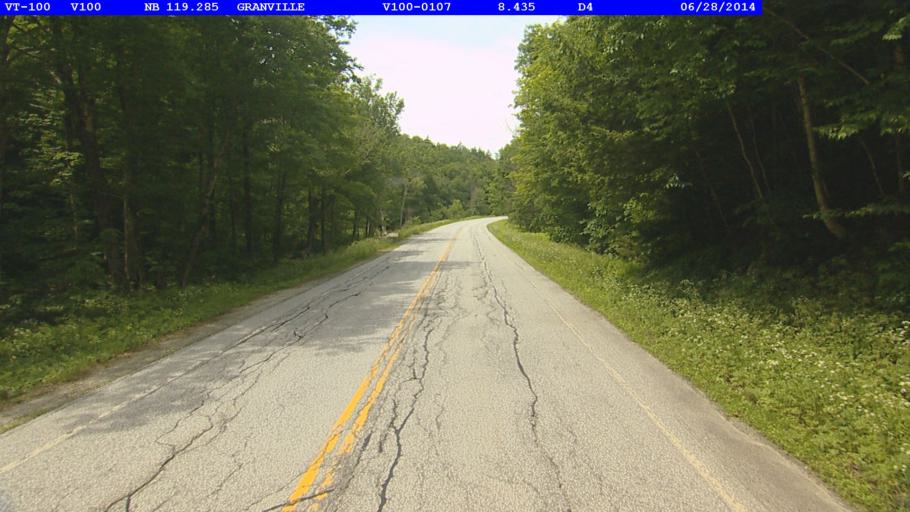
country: US
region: Vermont
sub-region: Washington County
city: Northfield
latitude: 44.0511
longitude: -72.8322
